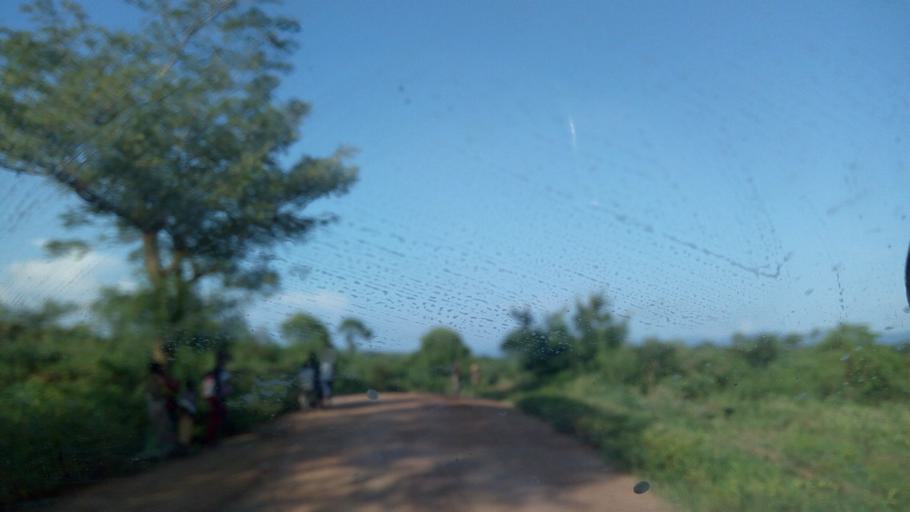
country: BI
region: Bururi
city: Rumonge
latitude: -4.1984
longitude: 29.0277
